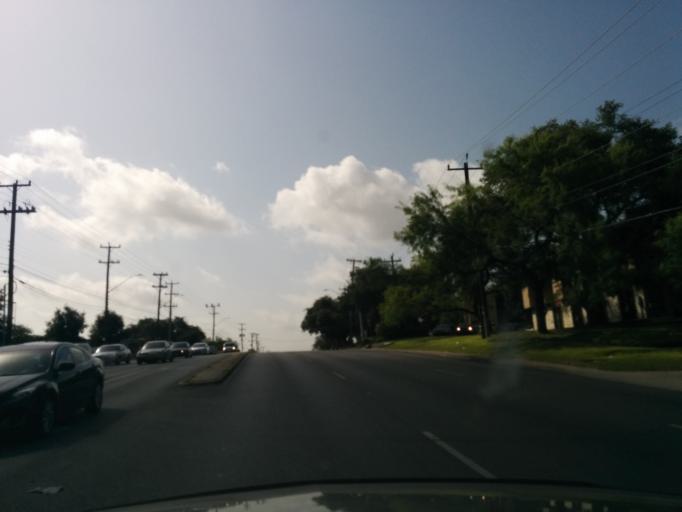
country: US
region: Texas
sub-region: Bexar County
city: Balcones Heights
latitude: 29.5042
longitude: -98.5838
